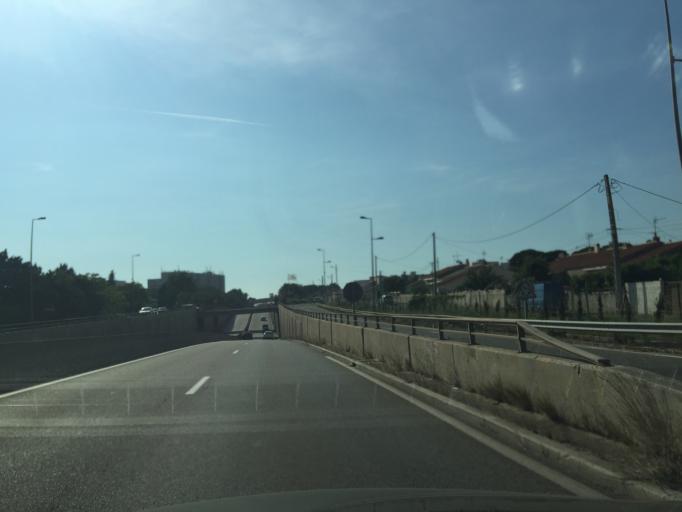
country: FR
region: Provence-Alpes-Cote d'Azur
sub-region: Departement des Bouches-du-Rhone
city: Port-de-Bouc
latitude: 43.4143
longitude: 4.9887
